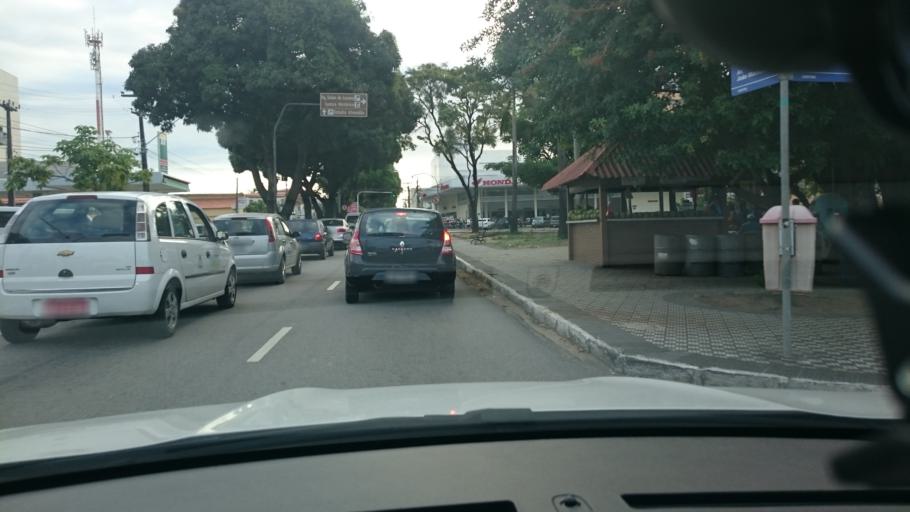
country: BR
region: Paraiba
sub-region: Joao Pessoa
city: Joao Pessoa
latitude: -7.1261
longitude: -34.8782
